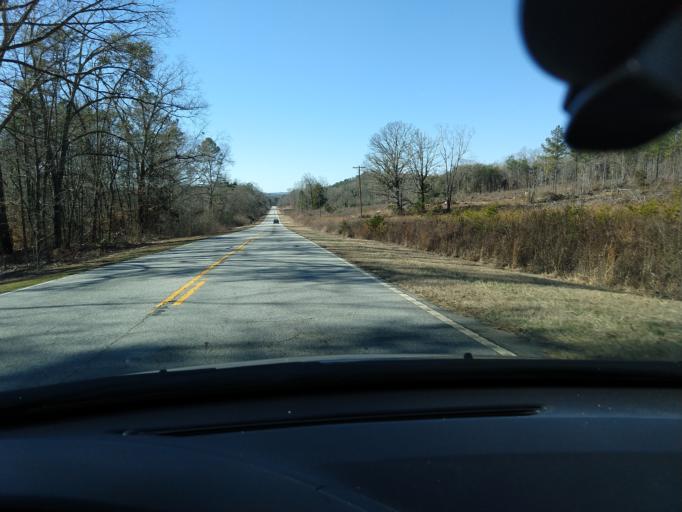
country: US
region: South Carolina
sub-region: Oconee County
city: Westminster
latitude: 34.6141
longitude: -83.1865
